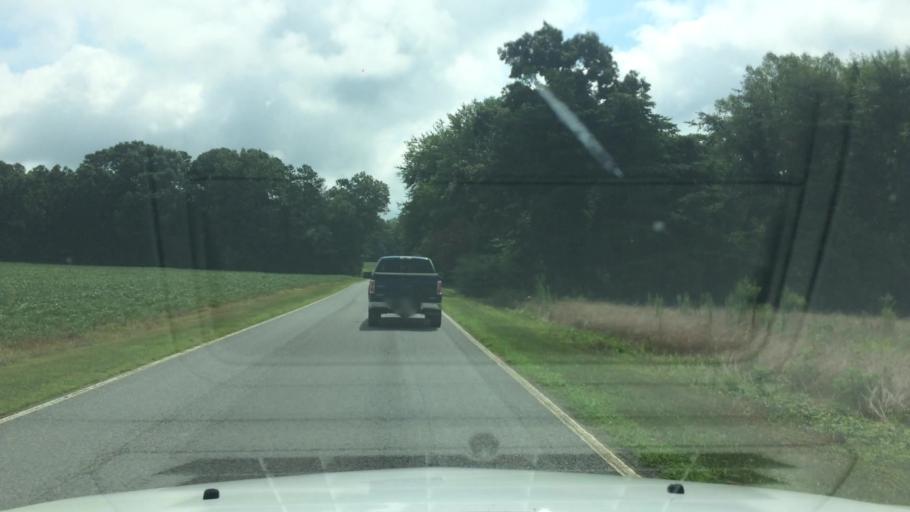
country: US
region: North Carolina
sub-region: Yadkin County
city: Jonesville
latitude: 36.0994
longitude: -80.8566
